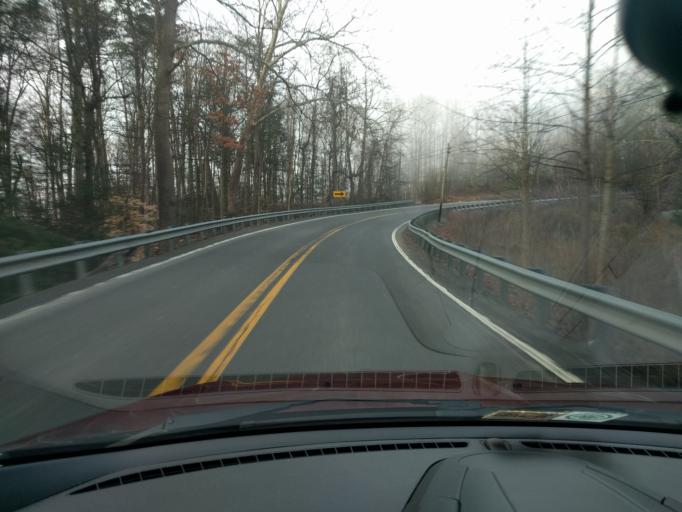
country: US
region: West Virginia
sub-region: Fayette County
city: Ansted
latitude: 38.1241
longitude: -81.1307
